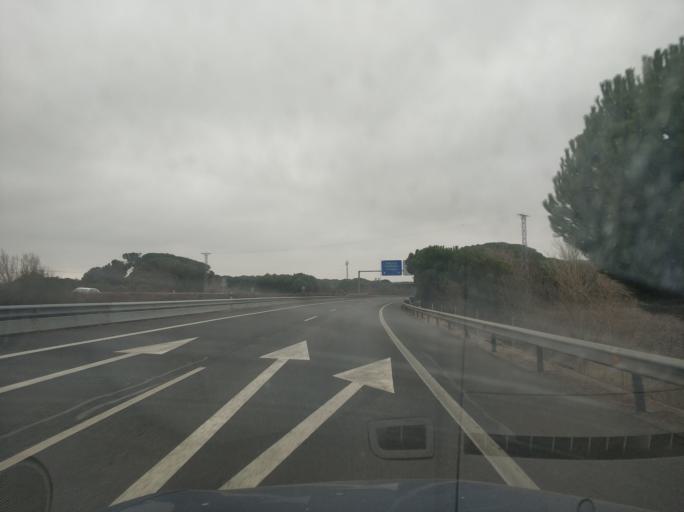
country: ES
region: Castille and Leon
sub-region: Provincia de Valladolid
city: Tordesillas
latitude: 41.4927
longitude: -5.0226
